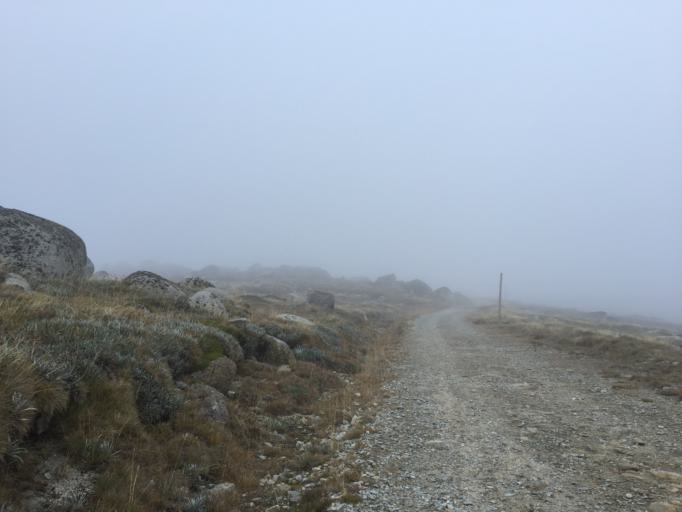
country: AU
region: New South Wales
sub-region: Snowy River
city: Jindabyne
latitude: -36.4523
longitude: 148.2868
